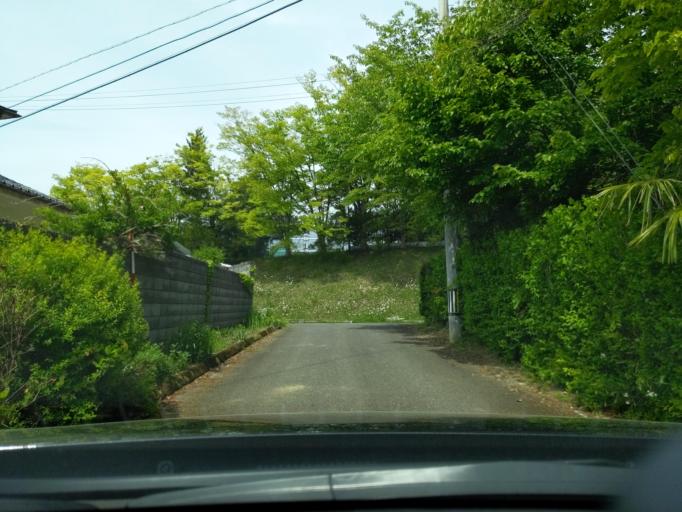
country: JP
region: Fukushima
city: Koriyama
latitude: 37.4062
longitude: 140.2733
